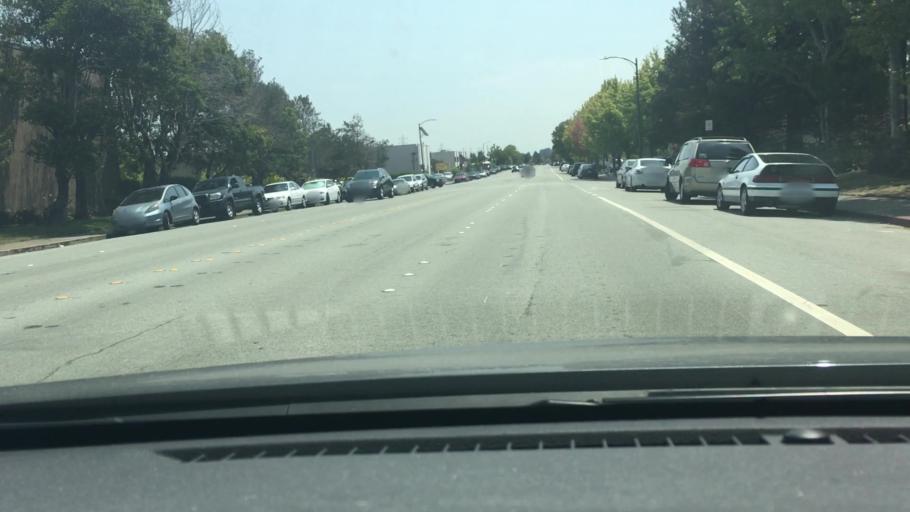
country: US
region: California
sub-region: San Mateo County
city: Millbrae
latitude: 37.5967
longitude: -122.3776
